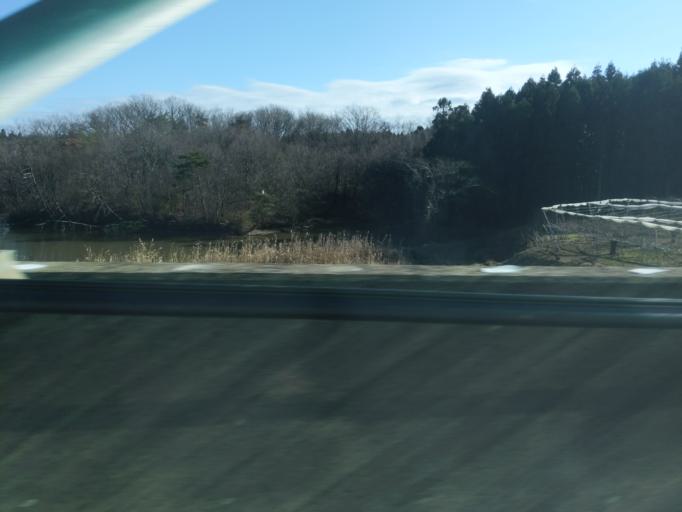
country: JP
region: Fukushima
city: Sukagawa
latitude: 37.3144
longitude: 140.3506
